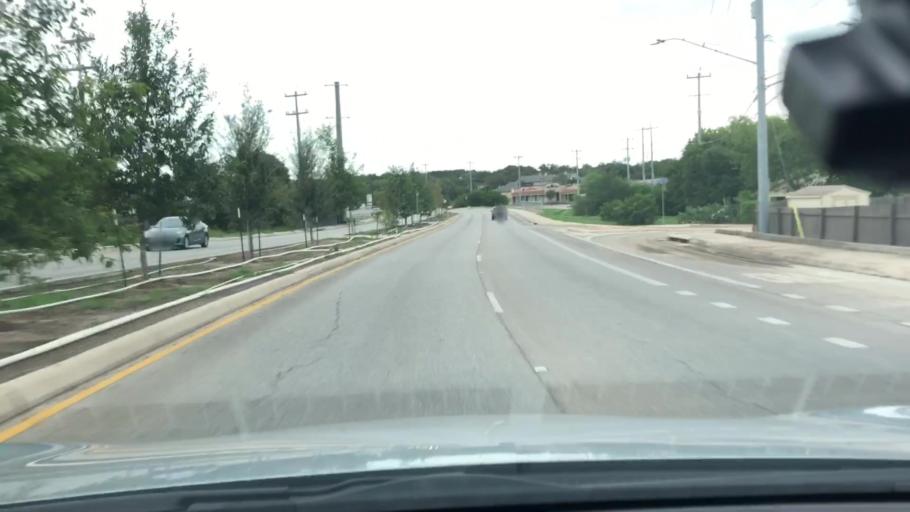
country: US
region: Texas
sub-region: Bexar County
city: Leon Valley
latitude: 29.4945
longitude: -98.6644
